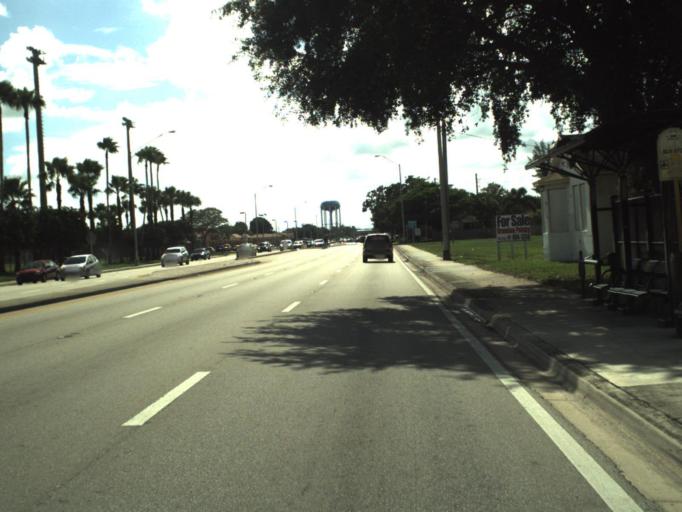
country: US
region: Florida
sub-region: Broward County
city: Dania Beach
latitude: 26.0335
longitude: -80.1539
